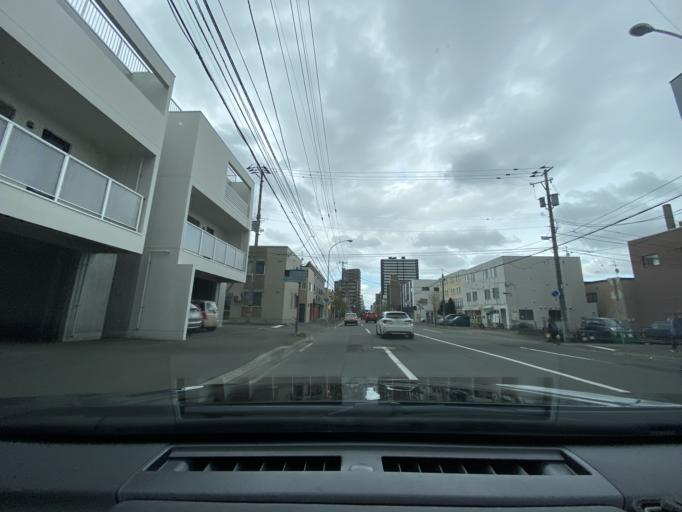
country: JP
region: Hokkaido
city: Sapporo
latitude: 43.0705
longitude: 141.2968
